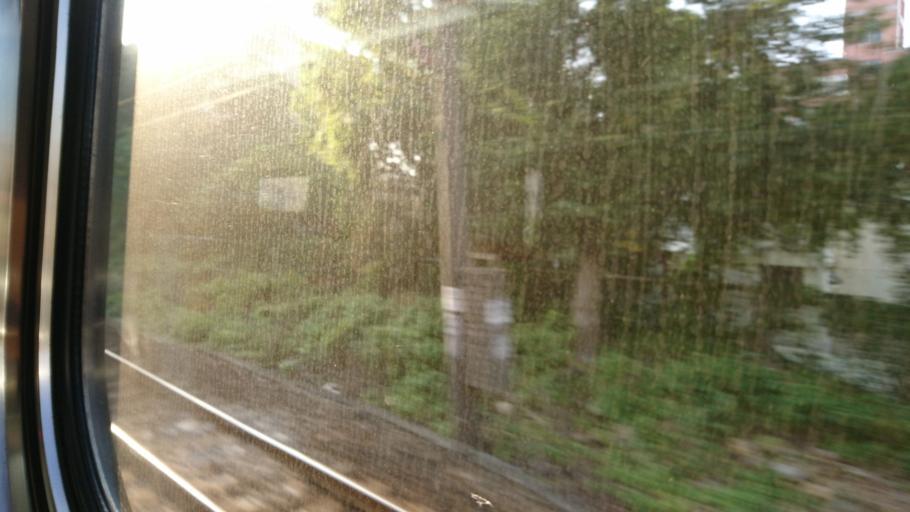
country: TW
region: Taiwan
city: Daxi
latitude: 24.9426
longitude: 121.2143
